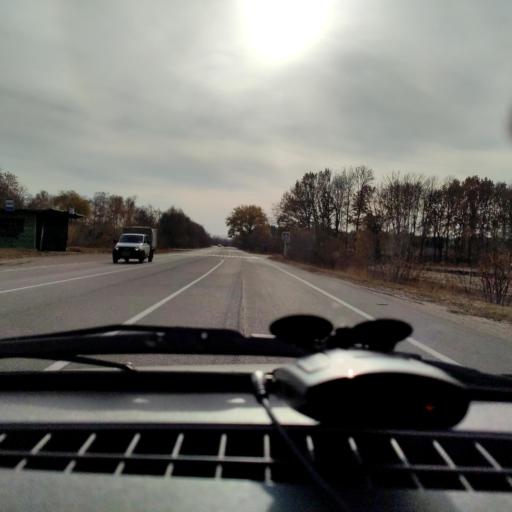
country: RU
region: Voronezj
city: Devitsa
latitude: 51.6021
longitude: 38.9716
